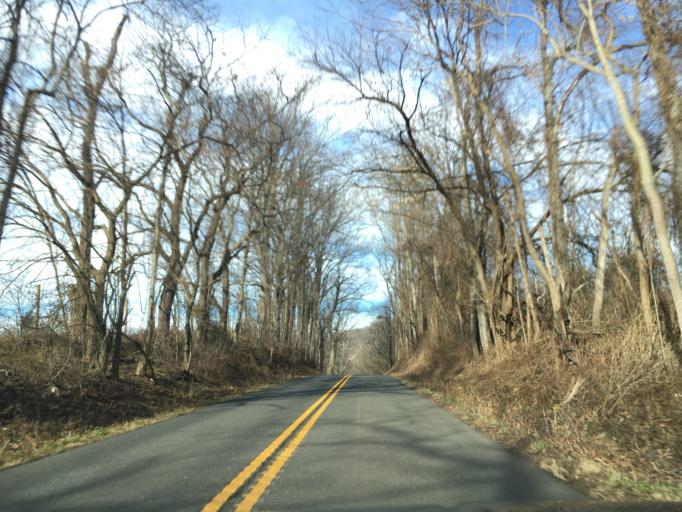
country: US
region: Virginia
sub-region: Warren County
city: Apple Mountain Lake
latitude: 38.8699
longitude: -77.9950
